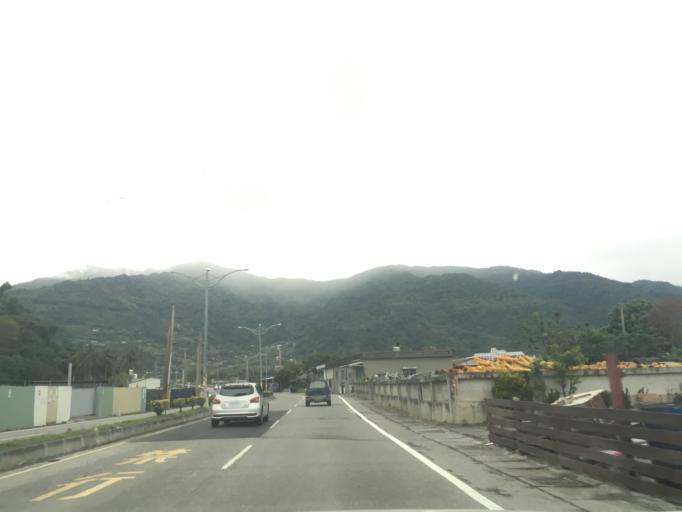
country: TW
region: Taiwan
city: Taitung City
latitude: 22.6982
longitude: 121.0425
